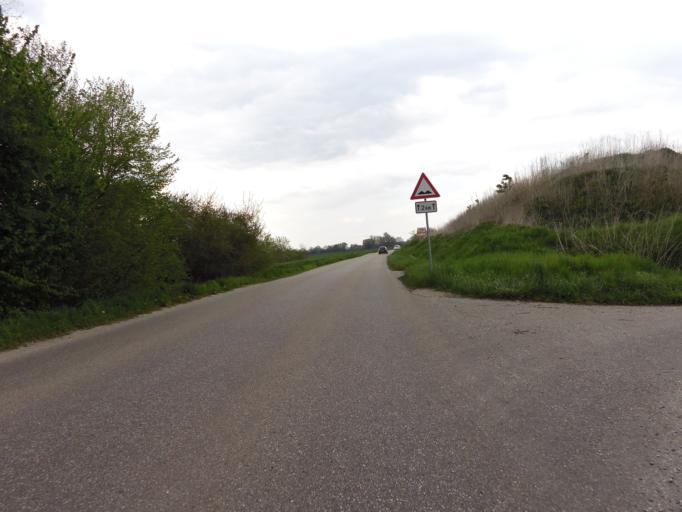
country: DE
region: Bavaria
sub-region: Upper Bavaria
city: Eitting
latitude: 48.3743
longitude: 11.9028
